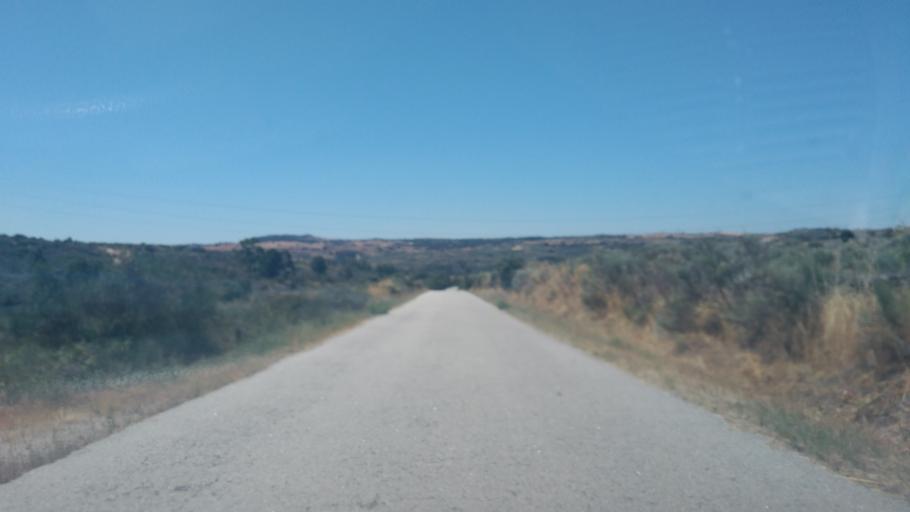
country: ES
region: Castille and Leon
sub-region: Provincia de Salamanca
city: Aldeadavila de la Ribera
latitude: 41.1980
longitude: -6.6472
